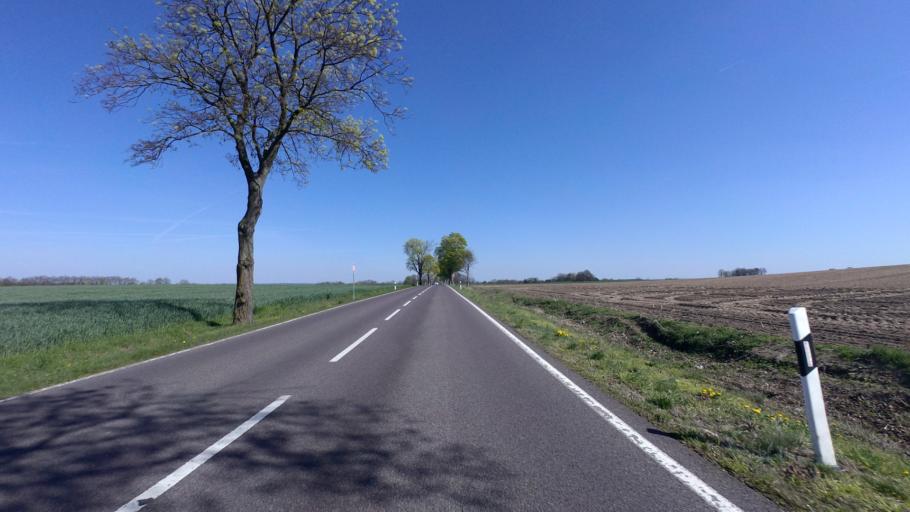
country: DE
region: Saxony-Anhalt
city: Kalbe
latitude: 52.6476
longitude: 11.3219
